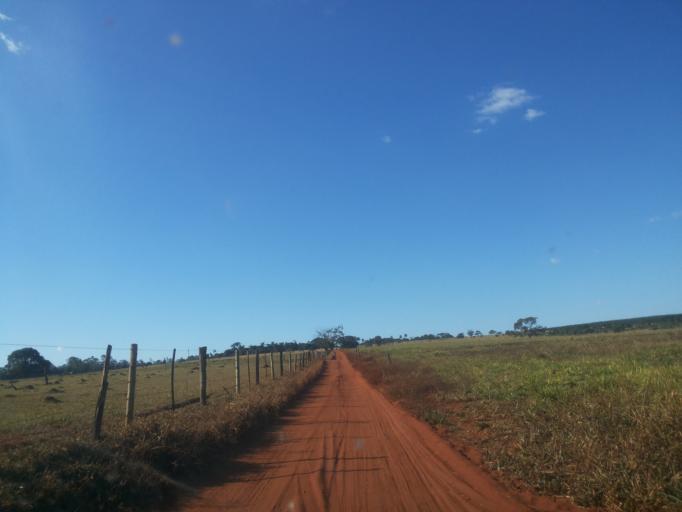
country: BR
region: Minas Gerais
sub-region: Centralina
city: Centralina
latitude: -18.7336
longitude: -49.1629
